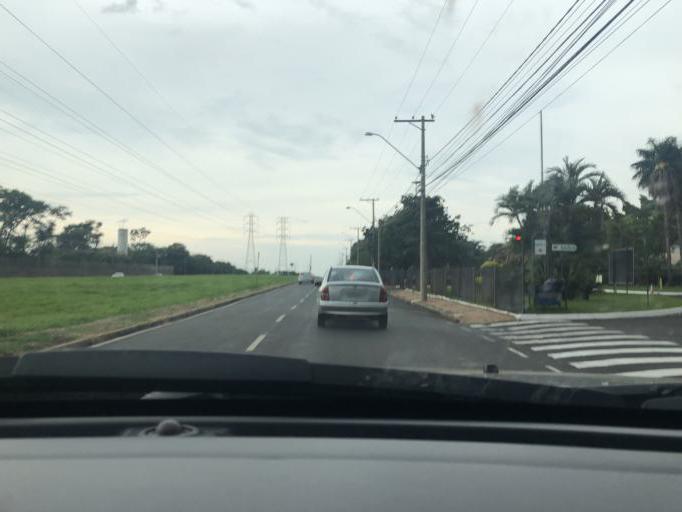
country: BR
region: Sao Paulo
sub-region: Sao Jose Do Rio Preto
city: Sao Jose do Rio Preto
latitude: -20.8445
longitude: -49.3914
